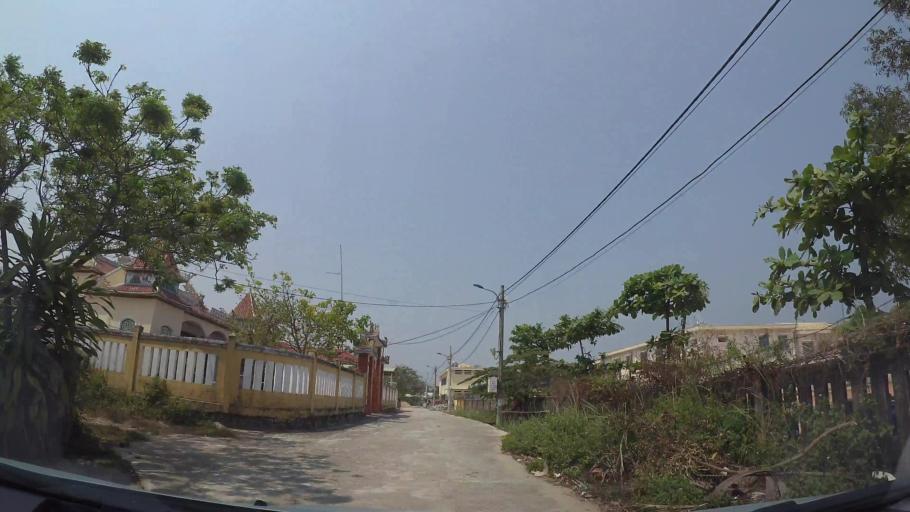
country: VN
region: Da Nang
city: Ngu Hanh Son
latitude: 15.9939
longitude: 108.2634
